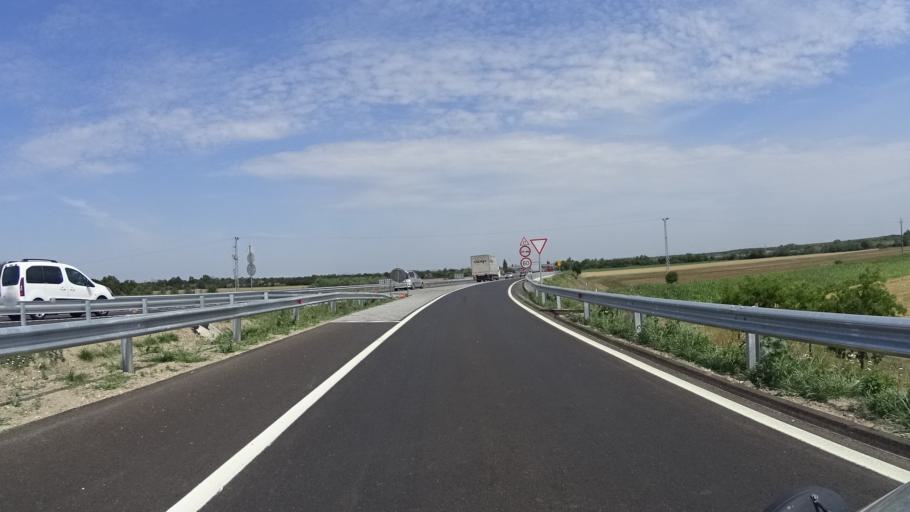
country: HU
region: Gyor-Moson-Sopron
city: Rajka
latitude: 47.9089
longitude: 17.1830
